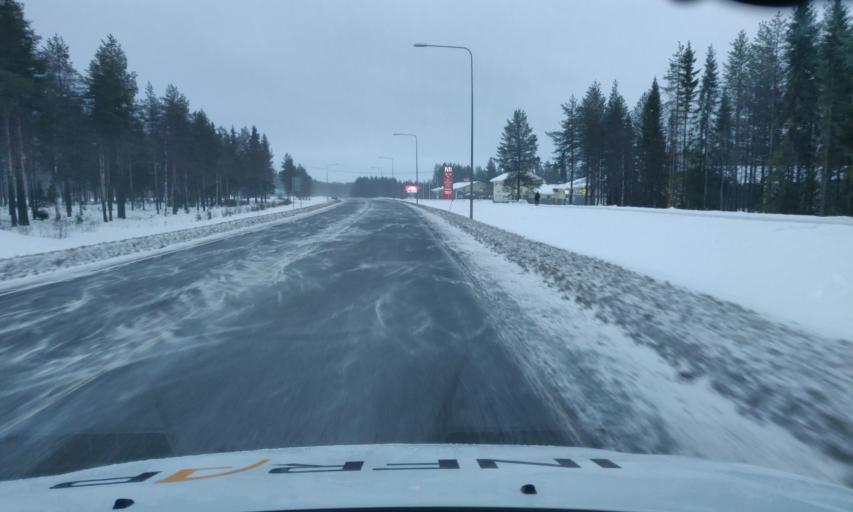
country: FI
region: Northern Ostrobothnia
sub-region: Koillismaa
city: Kuusamo
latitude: 65.9914
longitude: 29.1543
